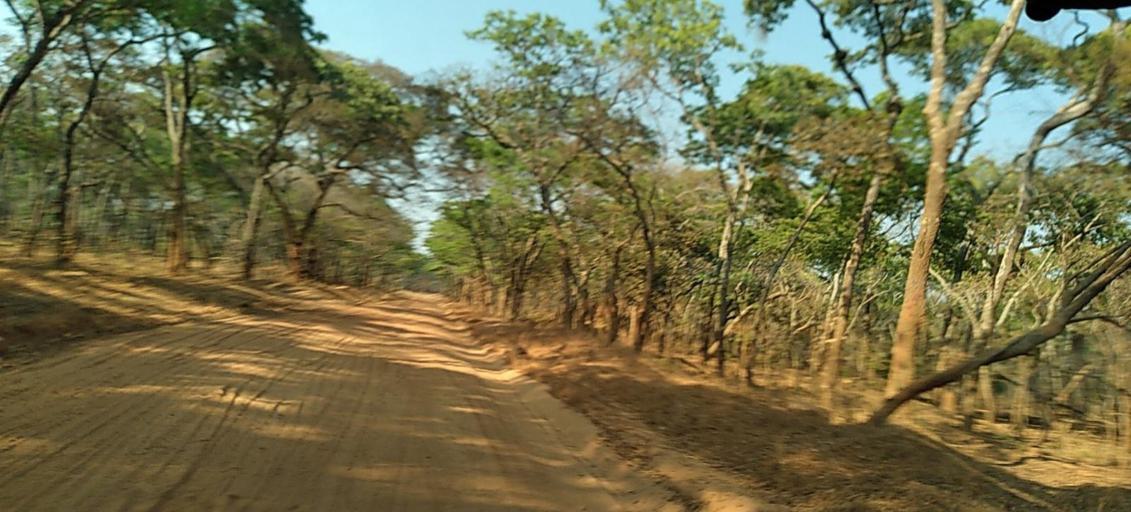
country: ZM
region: North-Western
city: Kasempa
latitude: -13.5777
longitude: 25.9906
